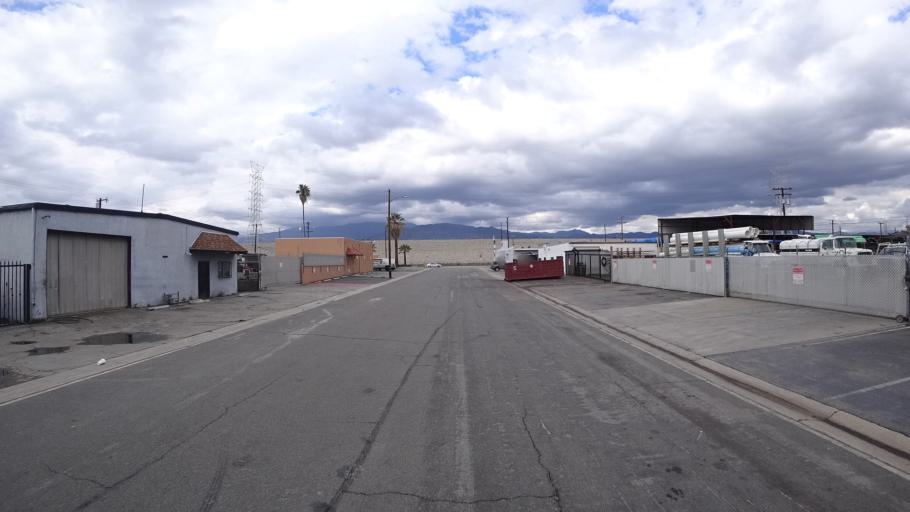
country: US
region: California
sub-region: Los Angeles County
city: Irwindale
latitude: 34.1059
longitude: -117.9479
